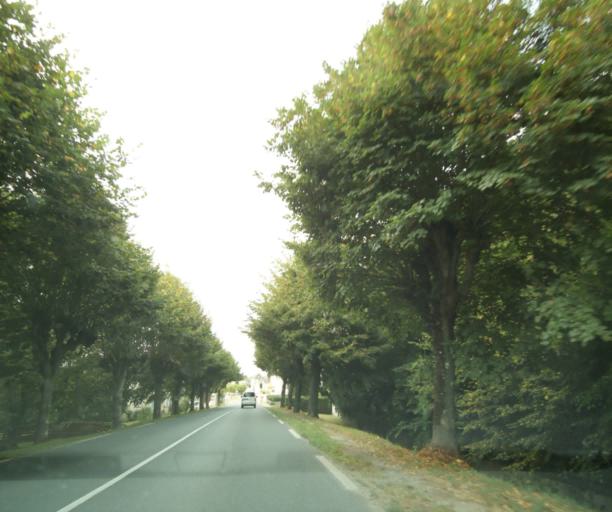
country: FR
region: Centre
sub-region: Departement de l'Indre
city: Chatillon-sur-Indre
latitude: 47.0180
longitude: 1.1098
